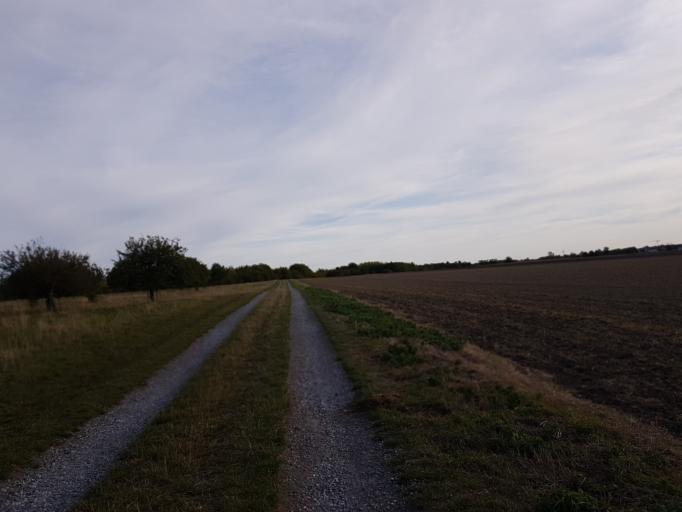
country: DE
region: Lower Saxony
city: Laatzen
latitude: 52.3495
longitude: 9.8514
